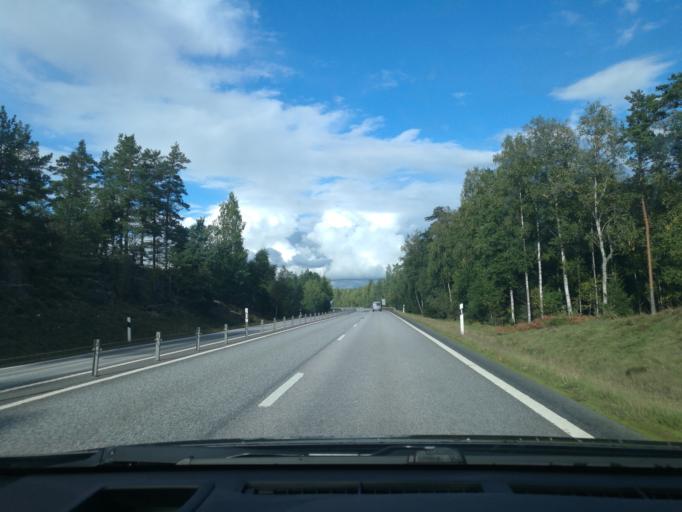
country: SE
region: OEstergoetland
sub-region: Norrkopings Kommun
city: Jursla
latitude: 58.7229
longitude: 16.1707
